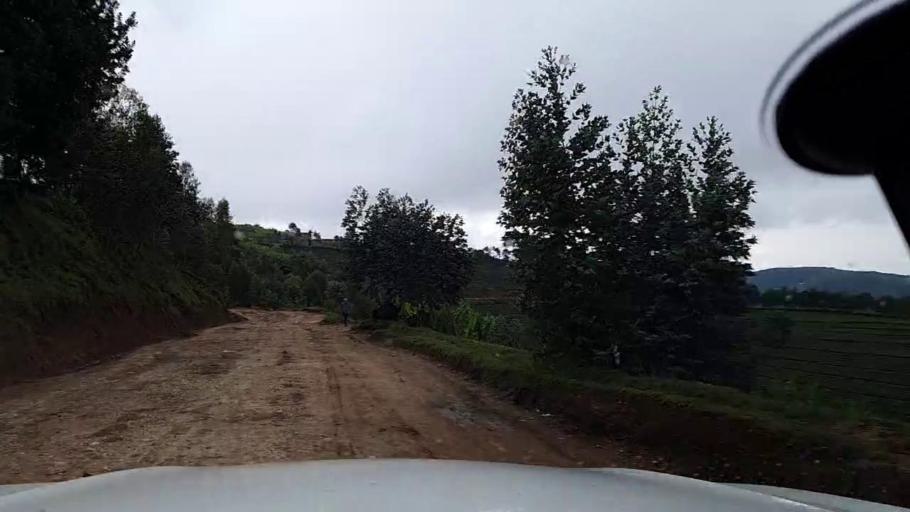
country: RW
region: Western Province
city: Kibuye
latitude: -2.0926
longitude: 29.4944
